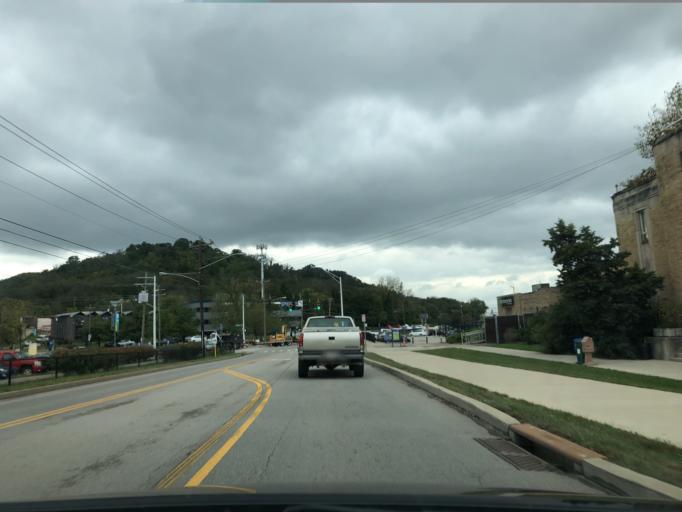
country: US
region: Kentucky
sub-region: Campbell County
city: Fort Thomas
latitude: 39.1034
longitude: -84.4301
